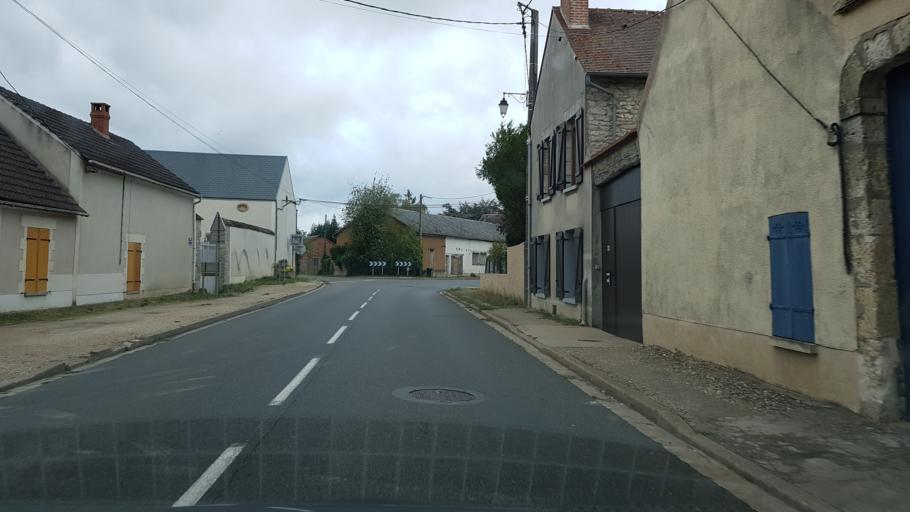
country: FR
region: Centre
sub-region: Departement du Loiret
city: Boynes
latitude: 48.1208
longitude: 2.3561
